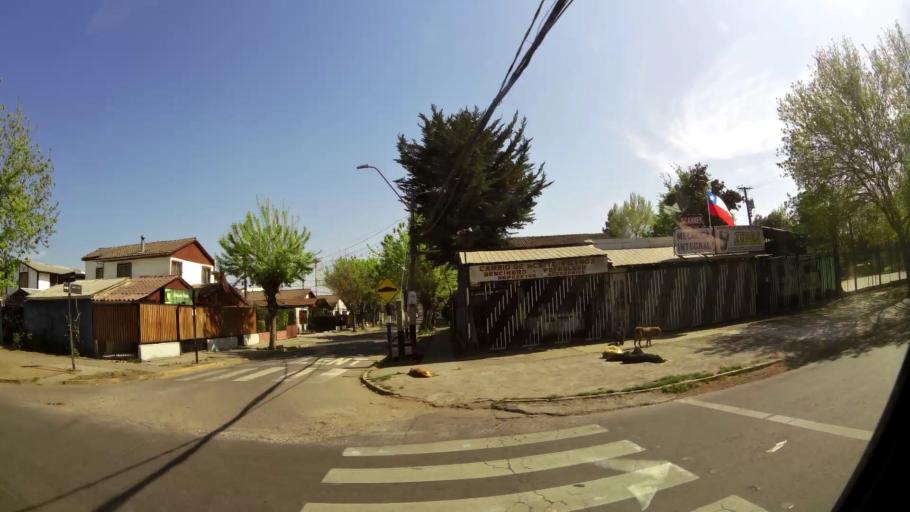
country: CL
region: Santiago Metropolitan
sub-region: Provincia de Santiago
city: Lo Prado
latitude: -33.4704
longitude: -70.7270
